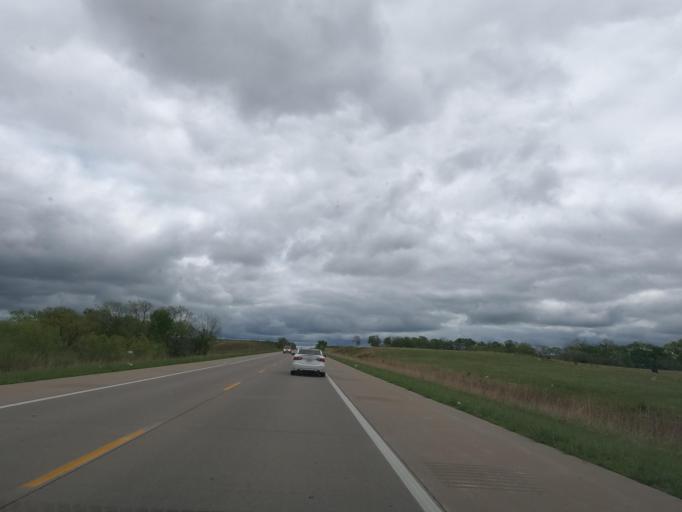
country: US
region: Kansas
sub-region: Wilson County
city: Neodesha
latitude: 37.3525
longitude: -95.6241
